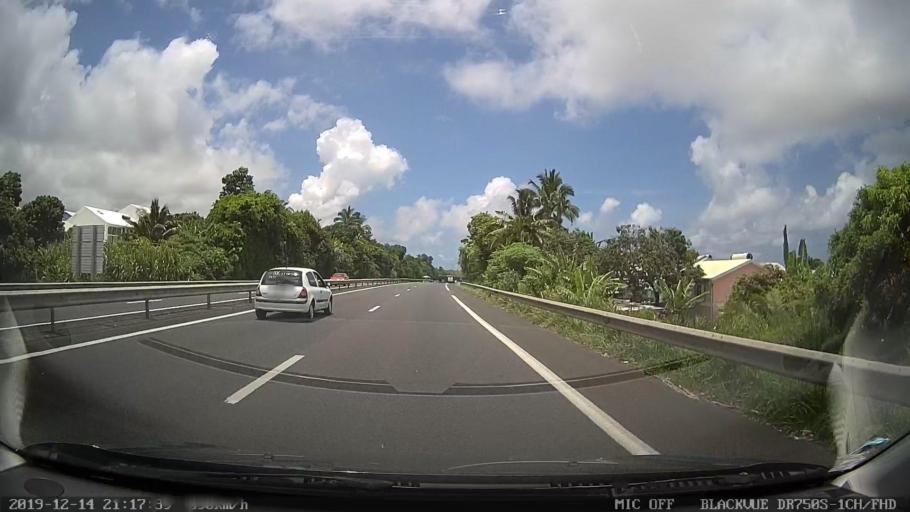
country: RE
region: Reunion
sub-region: Reunion
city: Saint-Andre
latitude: -20.9377
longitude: 55.6412
